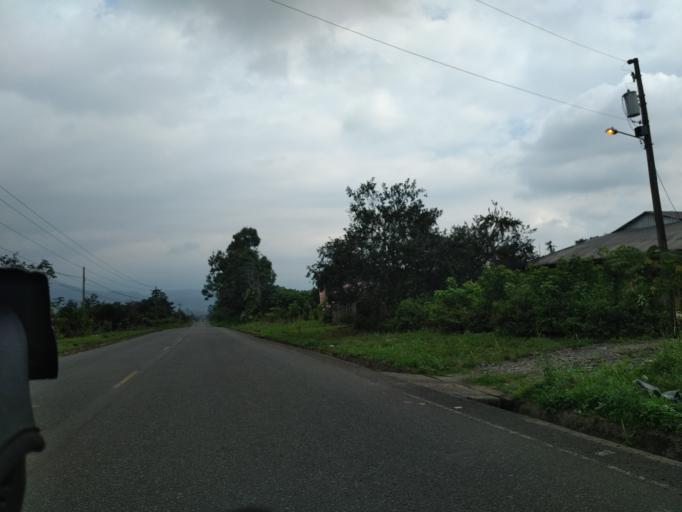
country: EC
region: Cotopaxi
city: La Mana
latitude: -0.8861
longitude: -79.1611
